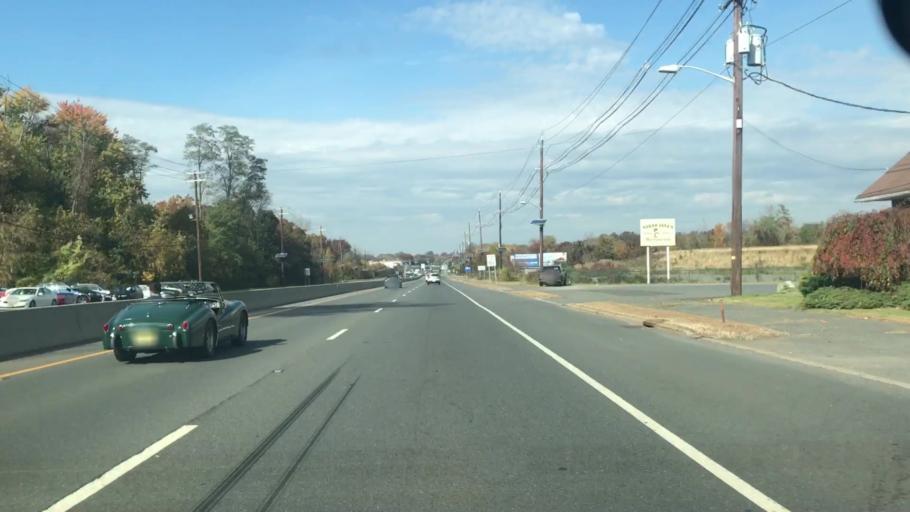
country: US
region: New Jersey
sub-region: Somerset County
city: Raritan
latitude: 40.5616
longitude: -74.6195
